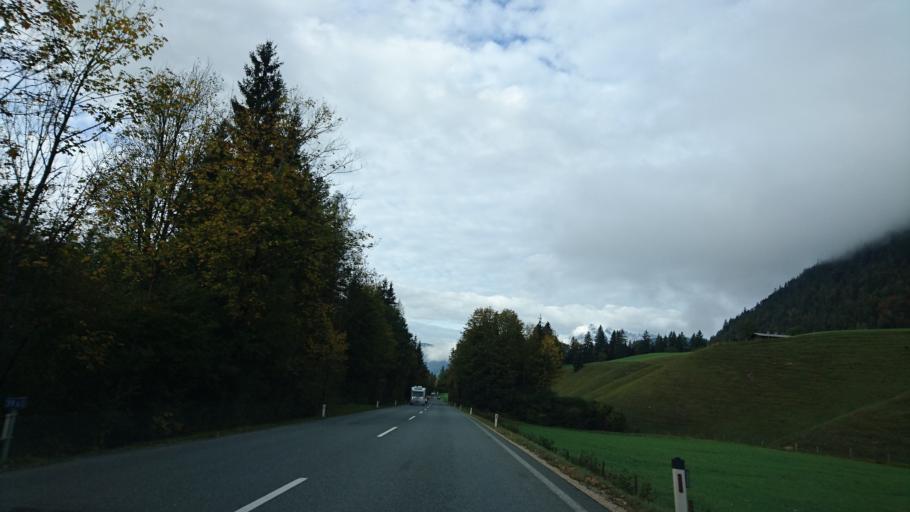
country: AT
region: Tyrol
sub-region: Politischer Bezirk Kitzbuhel
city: Waidring
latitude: 47.5881
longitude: 12.5164
